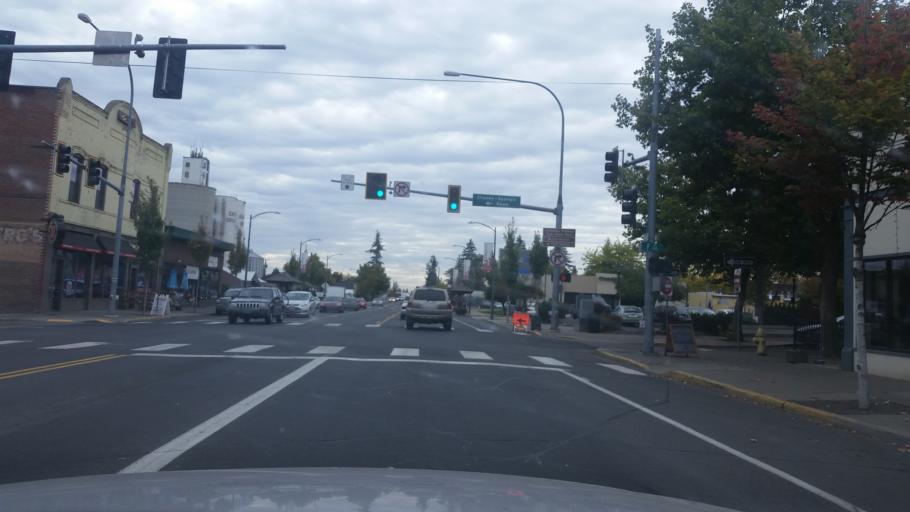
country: US
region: Washington
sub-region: Spokane County
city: Cheney
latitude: 47.4871
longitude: -117.5757
